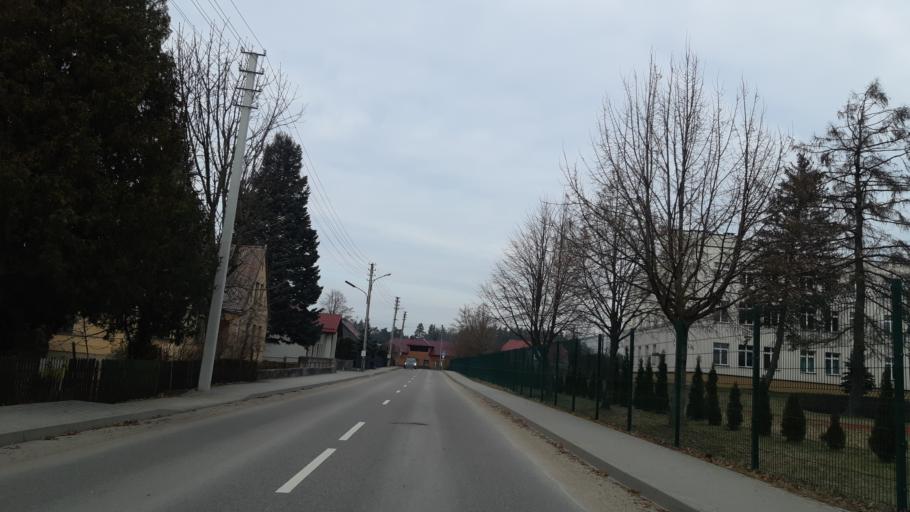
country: LT
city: Kazlu Ruda
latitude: 54.7528
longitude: 23.4957
